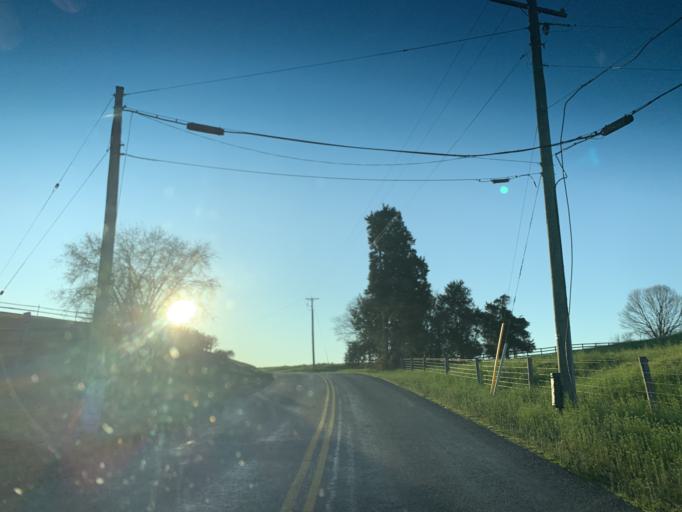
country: US
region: Maryland
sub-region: Harford County
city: South Bel Air
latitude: 39.5951
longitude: -76.2755
